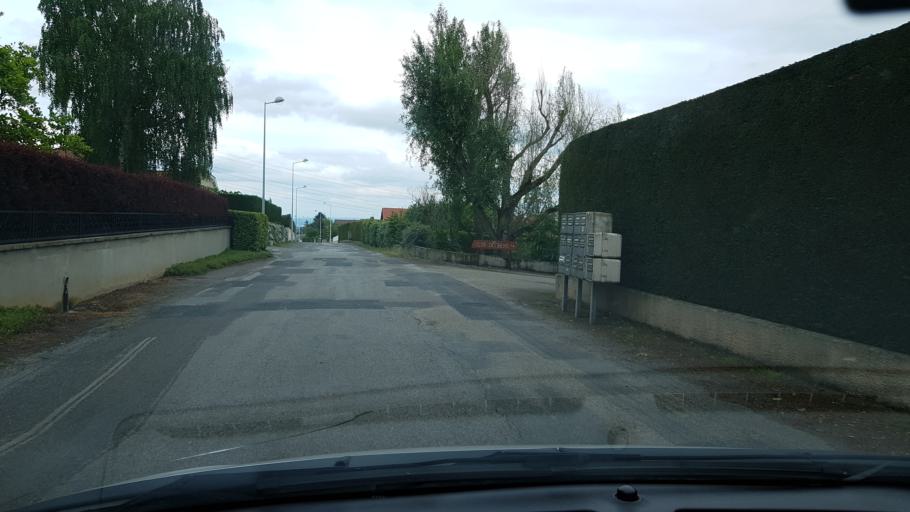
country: FR
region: Rhone-Alpes
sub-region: Departement du Rhone
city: Mornant
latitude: 45.6457
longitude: 4.6884
